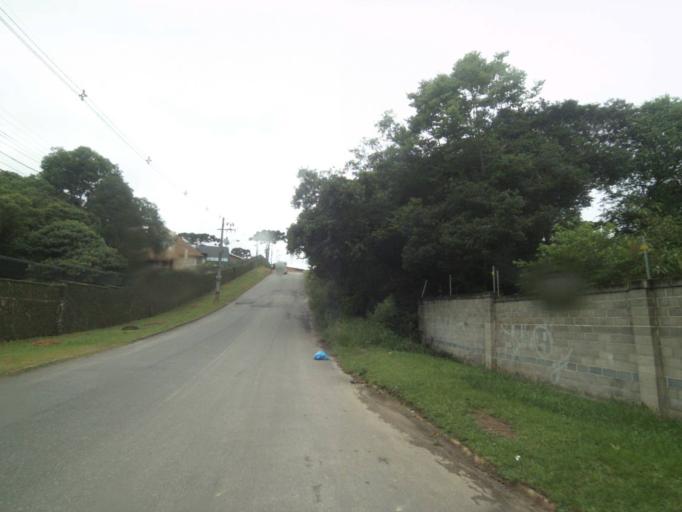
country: BR
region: Parana
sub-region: Curitiba
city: Curitiba
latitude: -25.4564
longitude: -49.3368
